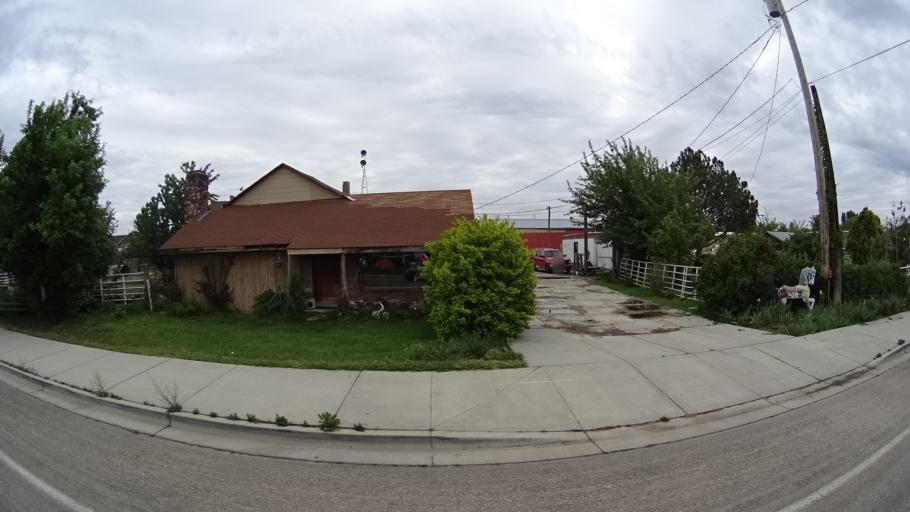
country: US
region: Idaho
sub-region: Ada County
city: Star
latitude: 43.6996
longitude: -116.4933
